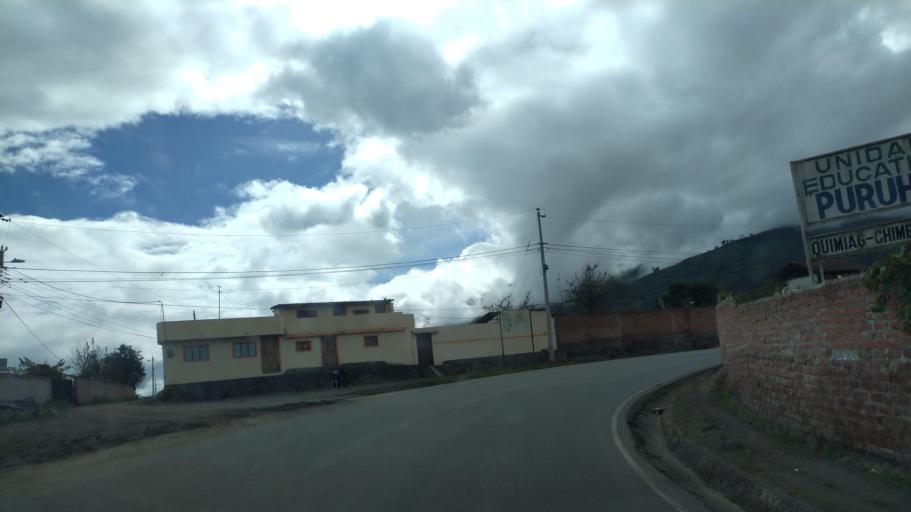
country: EC
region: Chimborazo
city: Riobamba
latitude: -1.6576
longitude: -78.5726
